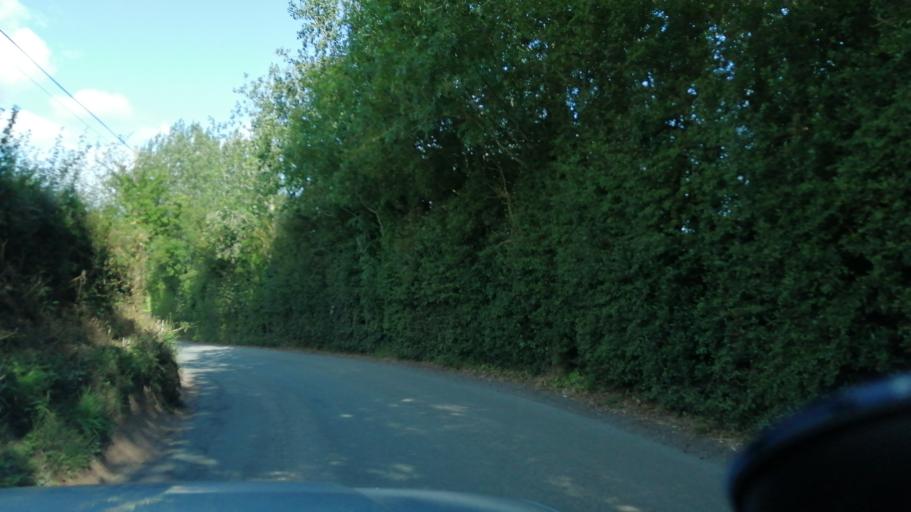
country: GB
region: England
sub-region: Herefordshire
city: Bridge Sollers
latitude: 52.0618
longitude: -2.8617
